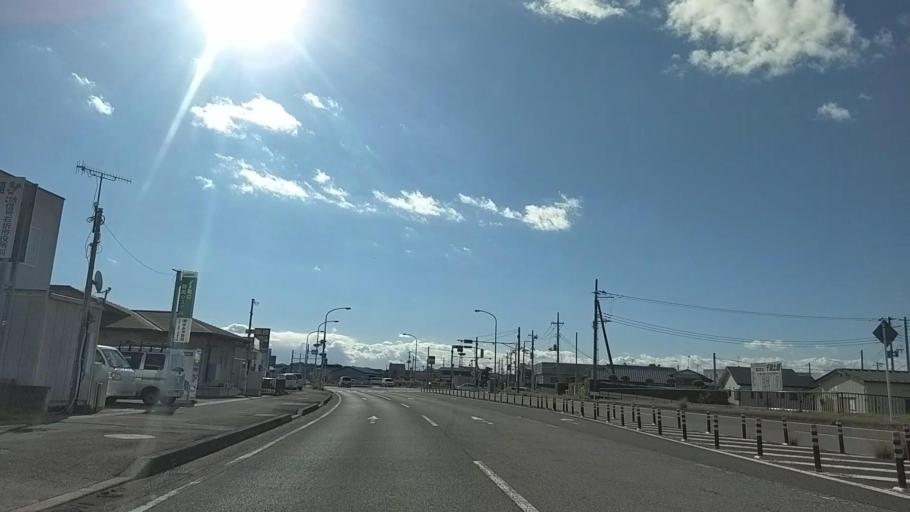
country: JP
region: Chiba
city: Tateyama
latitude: 35.0026
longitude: 139.8716
